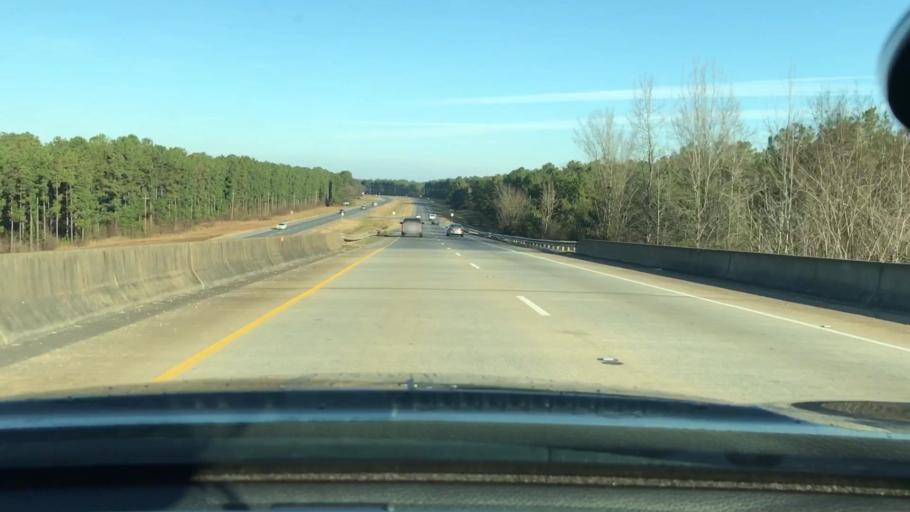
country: US
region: Alabama
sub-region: Talladega County
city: Childersburg
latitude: 33.2927
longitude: -86.3654
